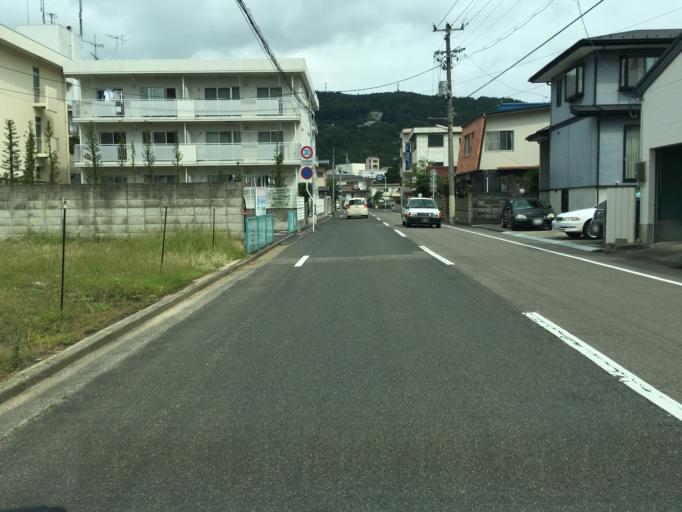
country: JP
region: Fukushima
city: Fukushima-shi
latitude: 37.7650
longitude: 140.4722
